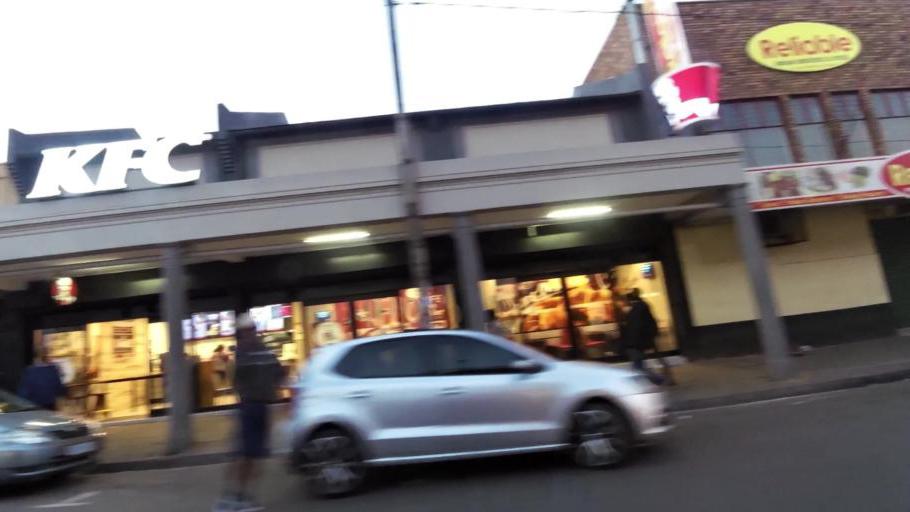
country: ZA
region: Gauteng
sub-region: City of Johannesburg Metropolitan Municipality
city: Johannesburg
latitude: -26.2052
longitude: 28.0179
